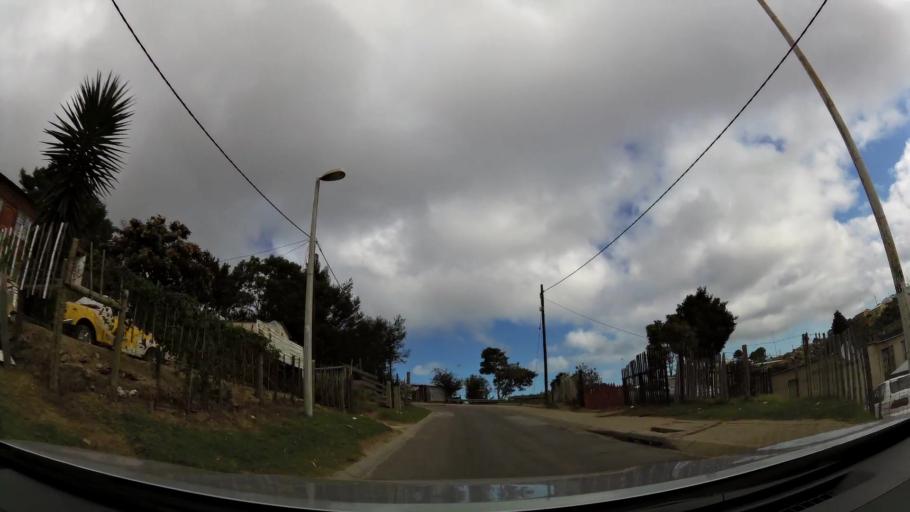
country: ZA
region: Western Cape
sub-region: Eden District Municipality
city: Knysna
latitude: -34.0339
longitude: 23.1040
